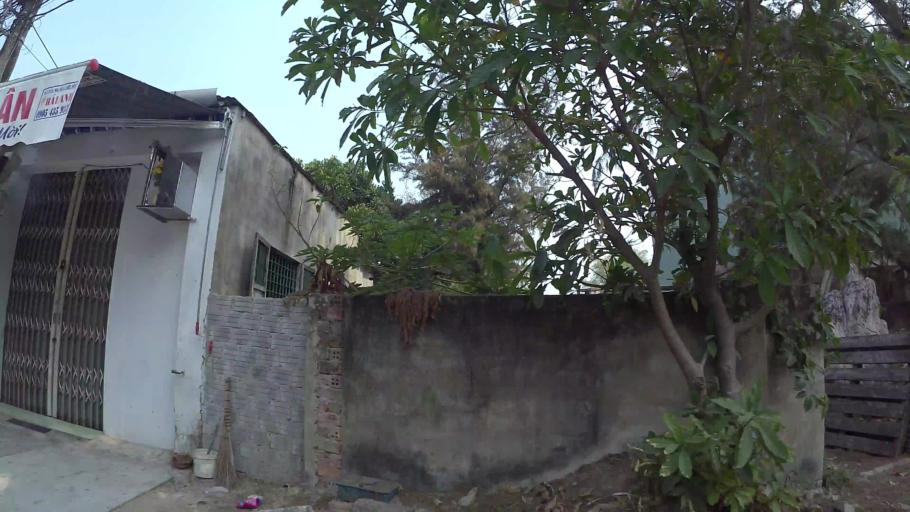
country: VN
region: Da Nang
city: Ngu Hanh Son
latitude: 15.9903
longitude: 108.2451
